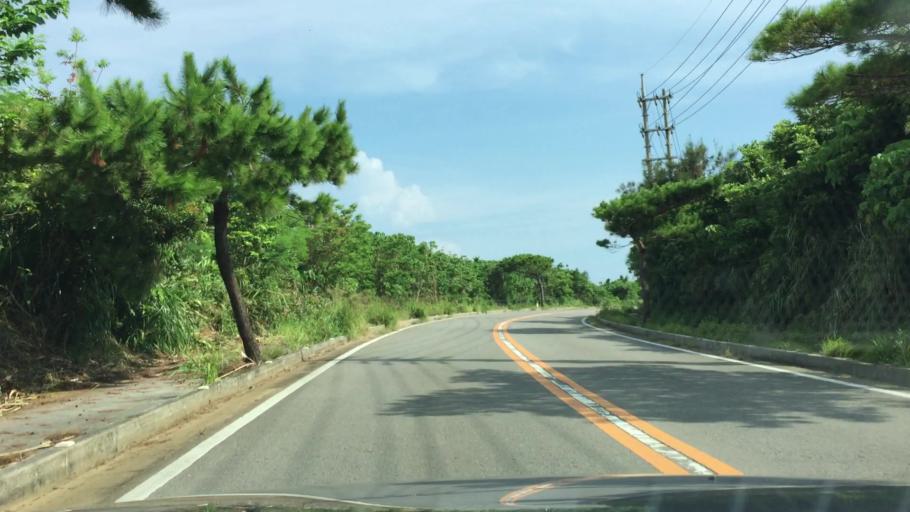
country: JP
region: Okinawa
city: Ishigaki
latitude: 24.4910
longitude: 124.2798
